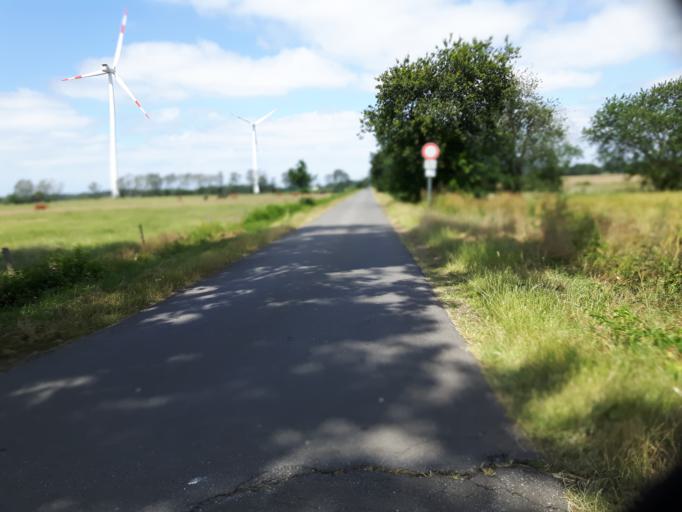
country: DE
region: Lower Saxony
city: Delmenhorst
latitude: 53.0081
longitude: 8.6354
